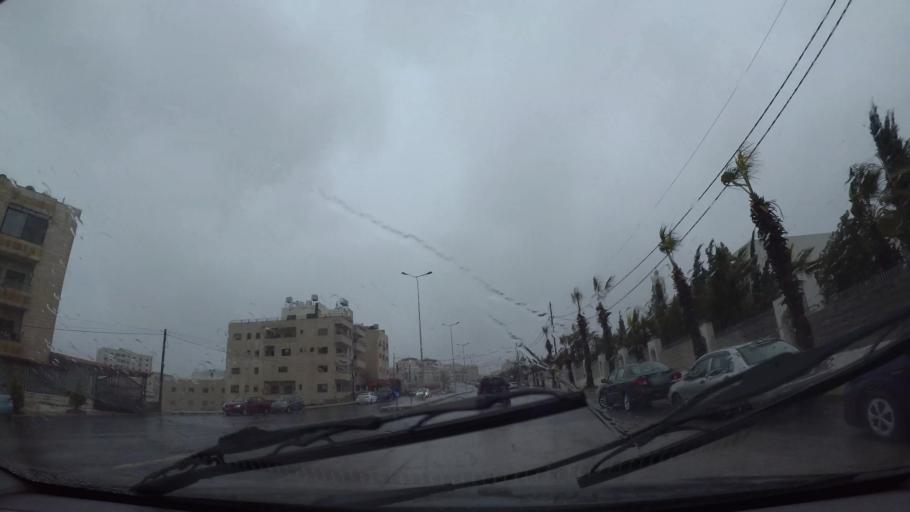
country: JO
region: Amman
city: Al Jubayhah
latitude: 32.0151
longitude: 35.8929
